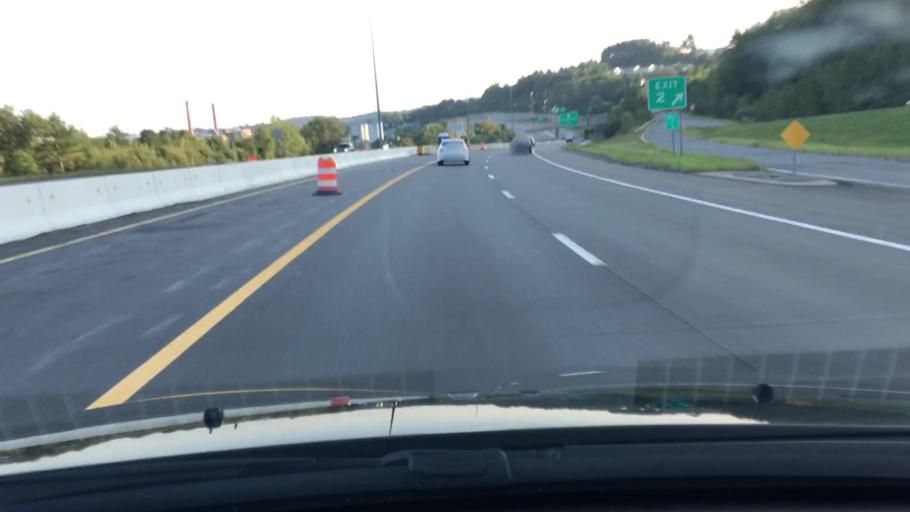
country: US
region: Massachusetts
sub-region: Worcester County
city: West Boylston
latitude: 42.3188
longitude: -71.8038
